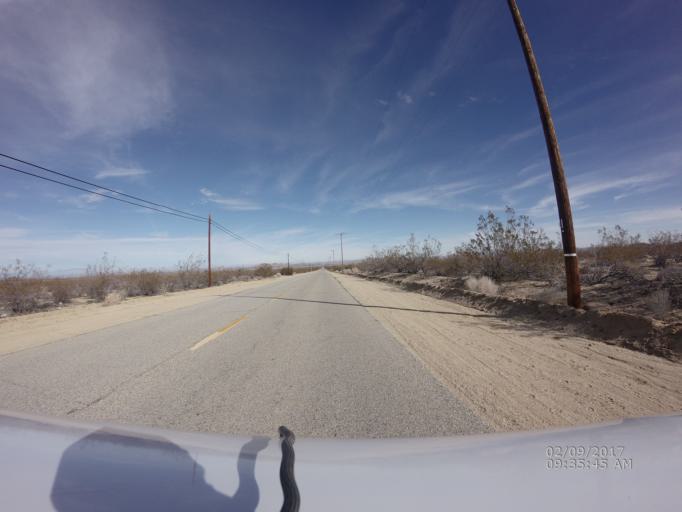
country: US
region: California
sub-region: Los Angeles County
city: Lake Los Angeles
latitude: 34.4964
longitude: -117.8353
